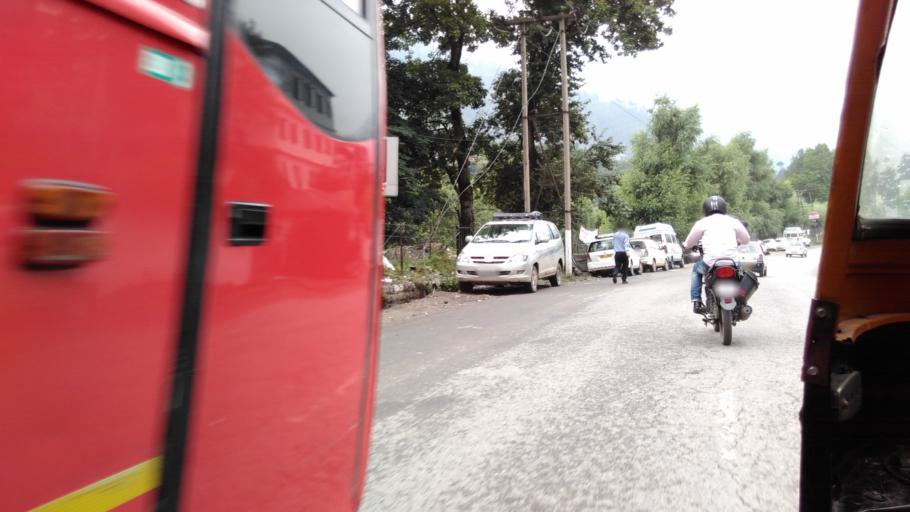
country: IN
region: Himachal Pradesh
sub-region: Kulu
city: Manali
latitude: 32.2274
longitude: 77.1890
